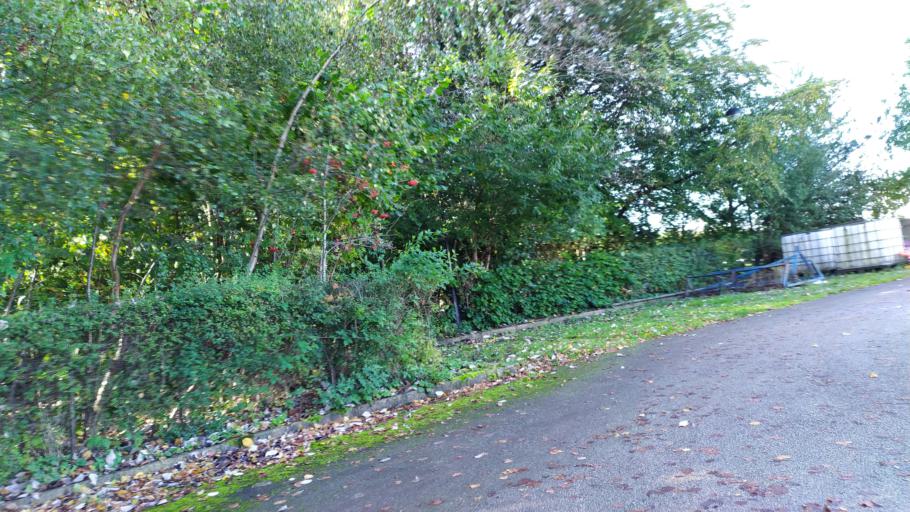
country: GB
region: England
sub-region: City and Borough of Leeds
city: Horsforth
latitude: 53.8259
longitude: -1.5983
